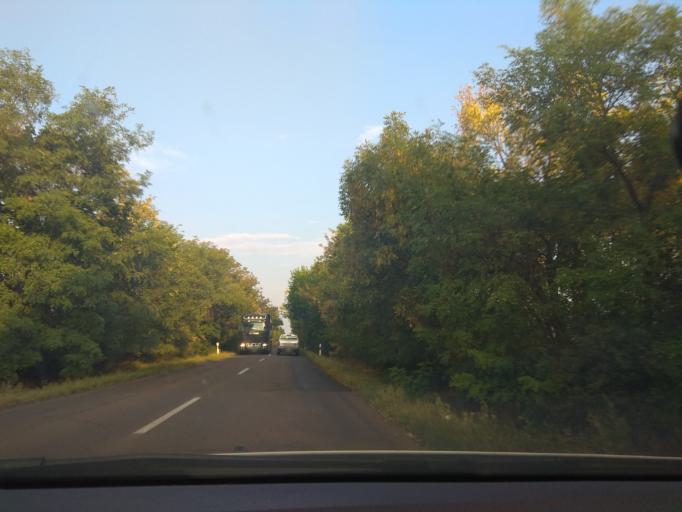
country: HU
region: Heves
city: Szihalom
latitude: 47.8202
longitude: 20.4985
